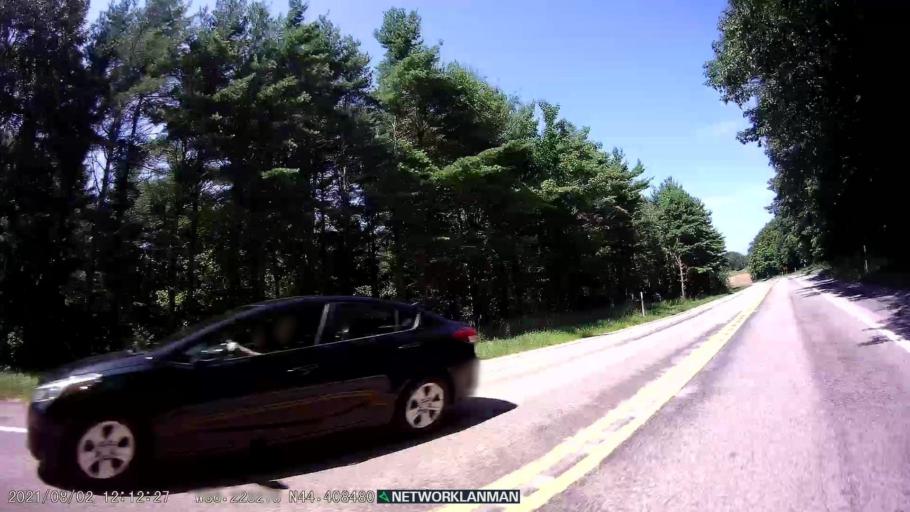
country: US
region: Michigan
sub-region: Manistee County
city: Manistee
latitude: 44.4089
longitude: -86.2233
